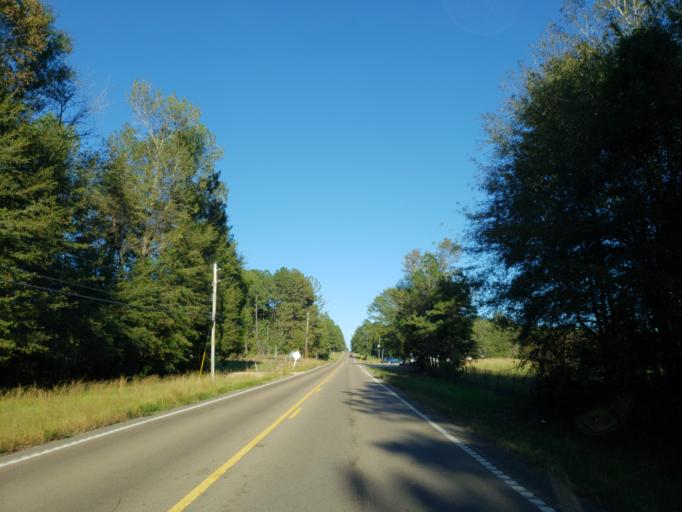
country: US
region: Mississippi
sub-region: Perry County
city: Richton
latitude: 31.3569
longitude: -88.9104
